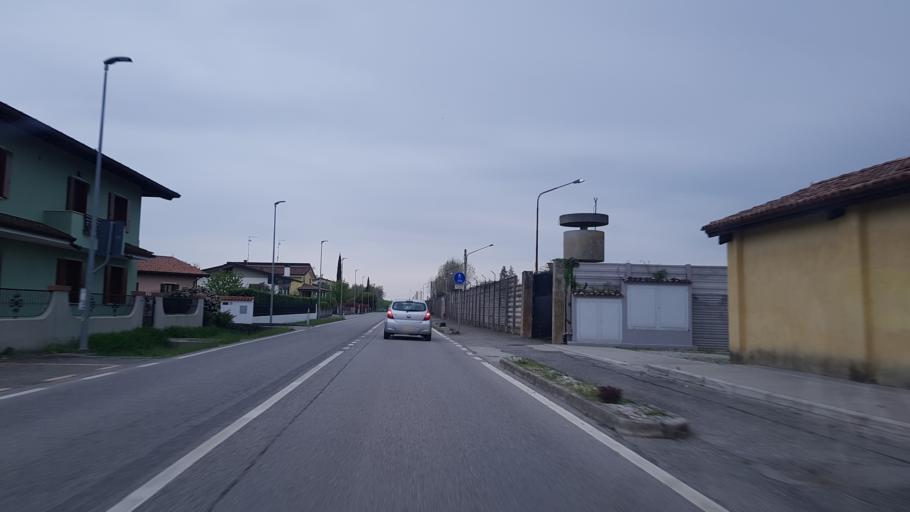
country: IT
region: Friuli Venezia Giulia
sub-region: Provincia di Udine
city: Visco
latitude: 45.8956
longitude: 13.3342
